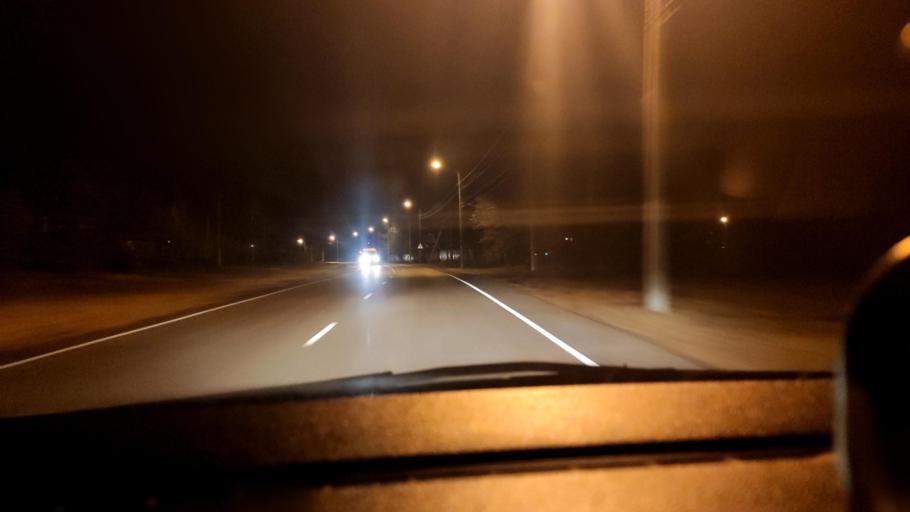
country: RU
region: Voronezj
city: Shilovo
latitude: 51.5502
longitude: 39.0806
